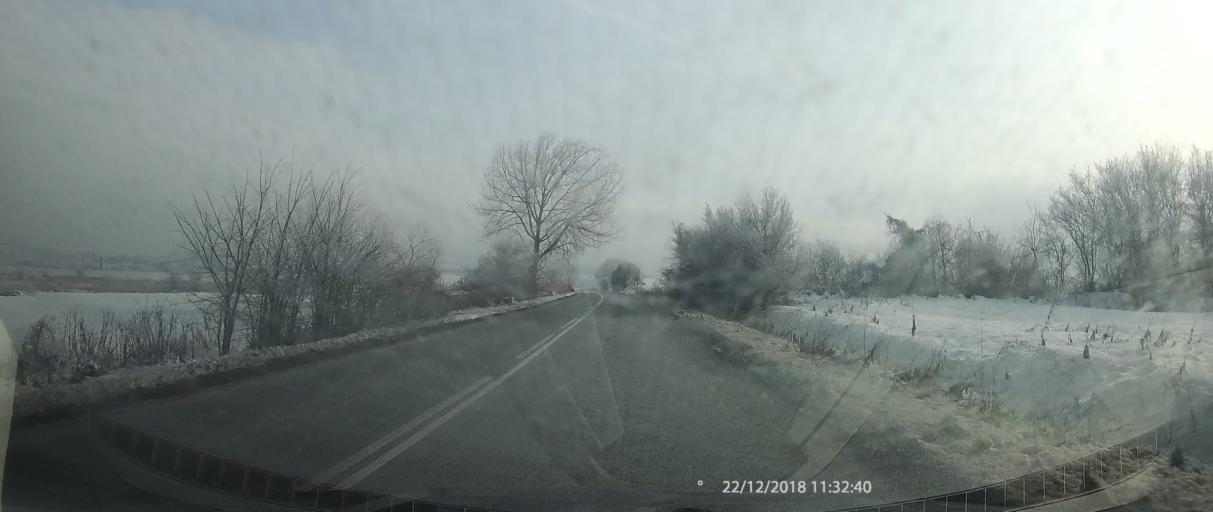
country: BG
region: Kyustendil
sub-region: Obshtina Dupnitsa
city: Dupnitsa
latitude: 42.2725
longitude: 23.0290
